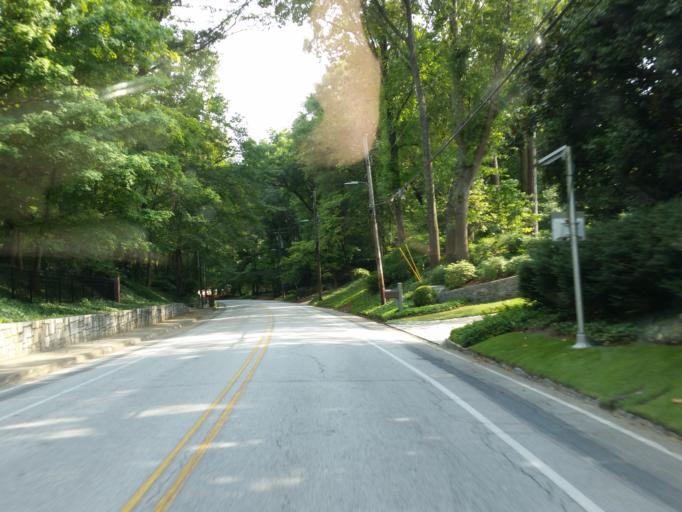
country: US
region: Georgia
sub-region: Cobb County
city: Vinings
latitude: 33.8274
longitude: -84.4165
